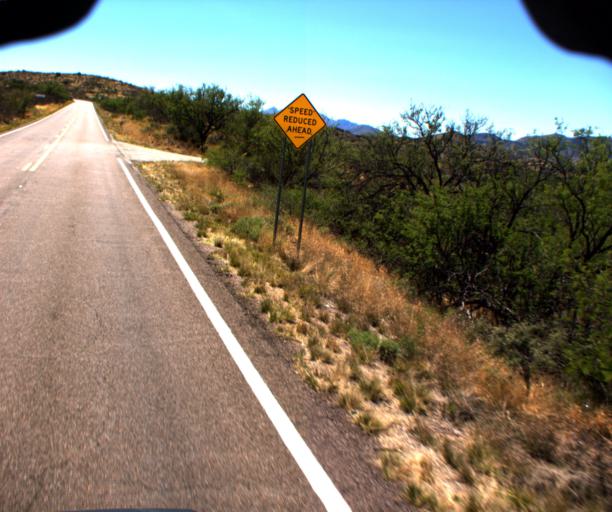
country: US
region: Arizona
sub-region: Pima County
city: Corona de Tucson
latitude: 31.8509
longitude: -110.6975
